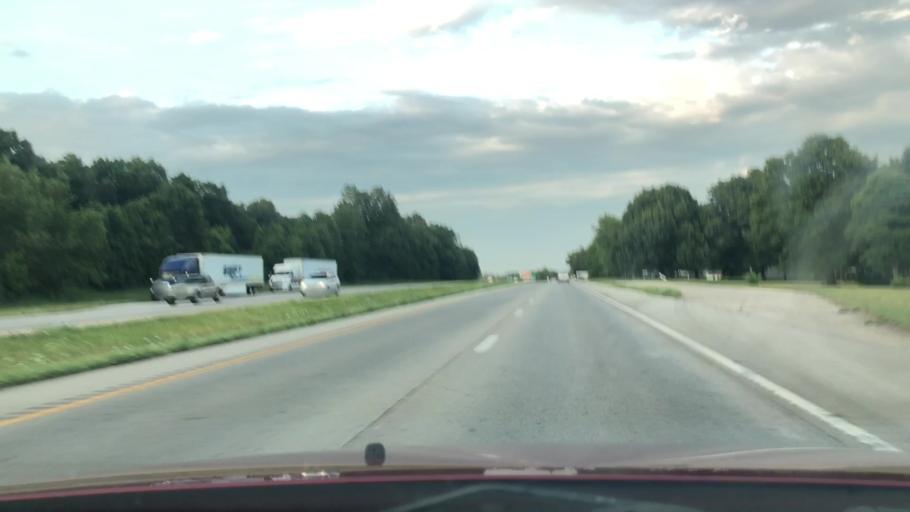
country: US
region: Missouri
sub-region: Greene County
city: Republic
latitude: 37.1411
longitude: -93.4386
